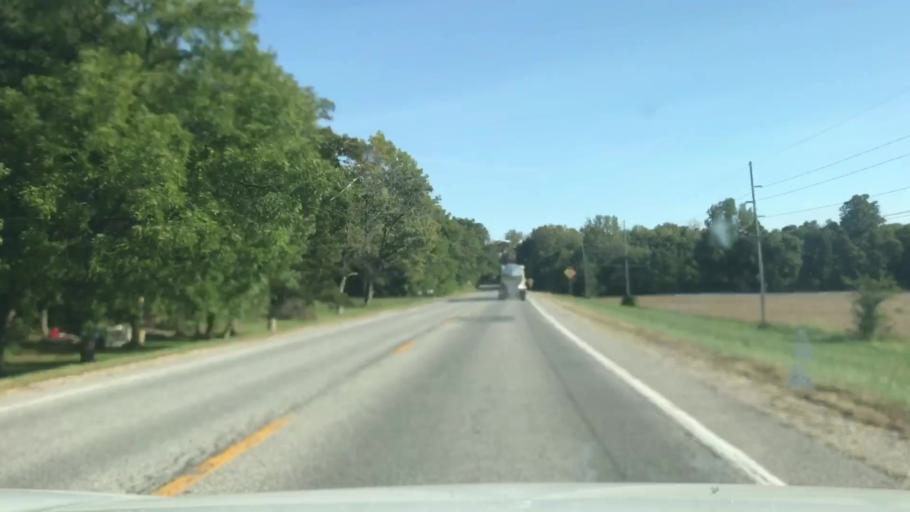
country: US
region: Illinois
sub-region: Adams County
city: Quincy
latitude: 39.8458
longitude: -91.3750
